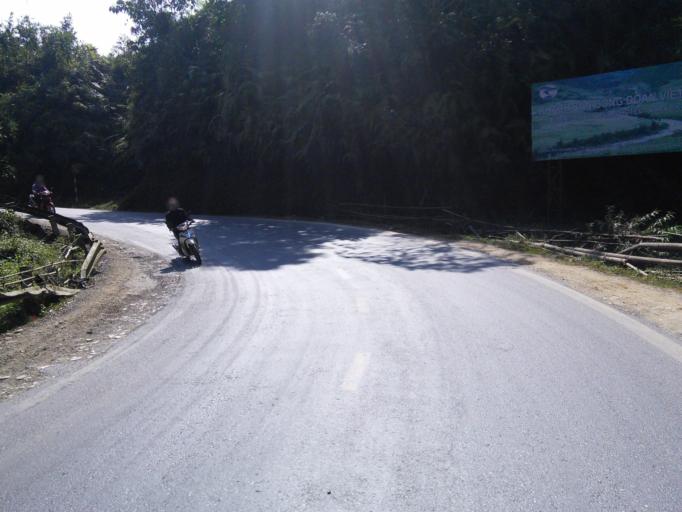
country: VN
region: Lao Cai
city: Sa Pa
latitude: 22.3580
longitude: 103.8627
